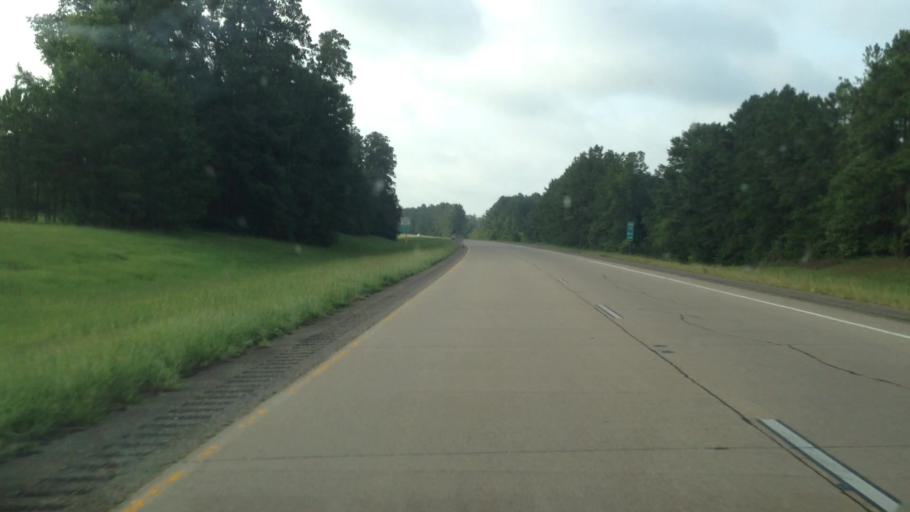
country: US
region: Louisiana
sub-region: Rapides Parish
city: Lecompte
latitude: 31.0364
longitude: -92.4138
